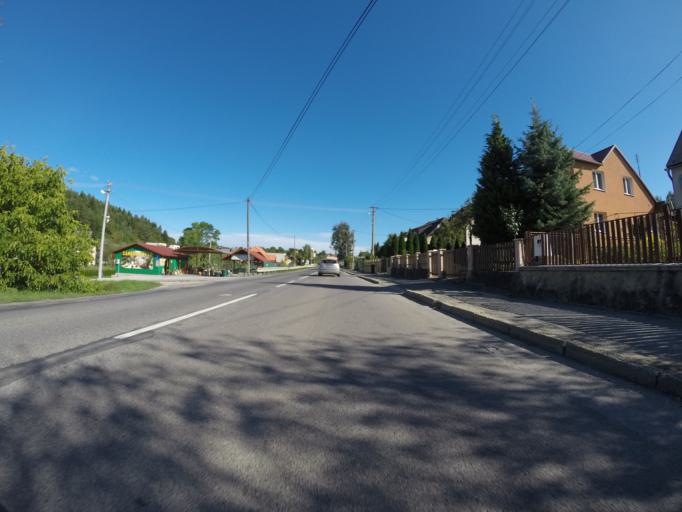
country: SK
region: Trenciansky
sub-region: Okres Povazska Bystrica
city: Povazska Bystrica
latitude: 49.0740
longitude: 18.4035
